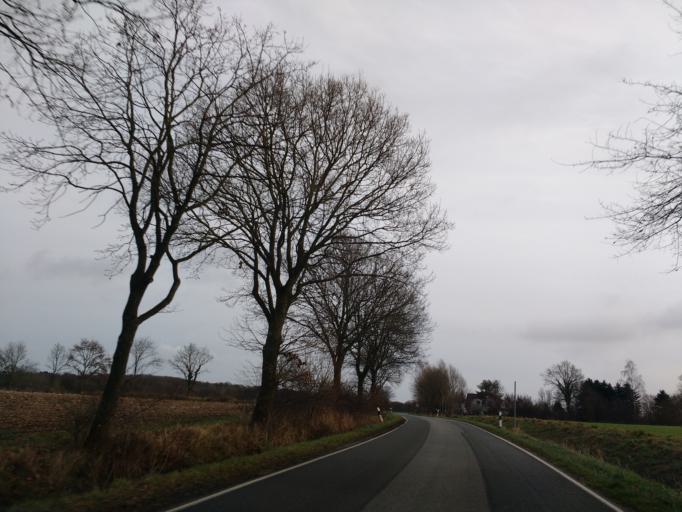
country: DE
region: Schleswig-Holstein
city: Susel
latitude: 54.0126
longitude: 10.6685
